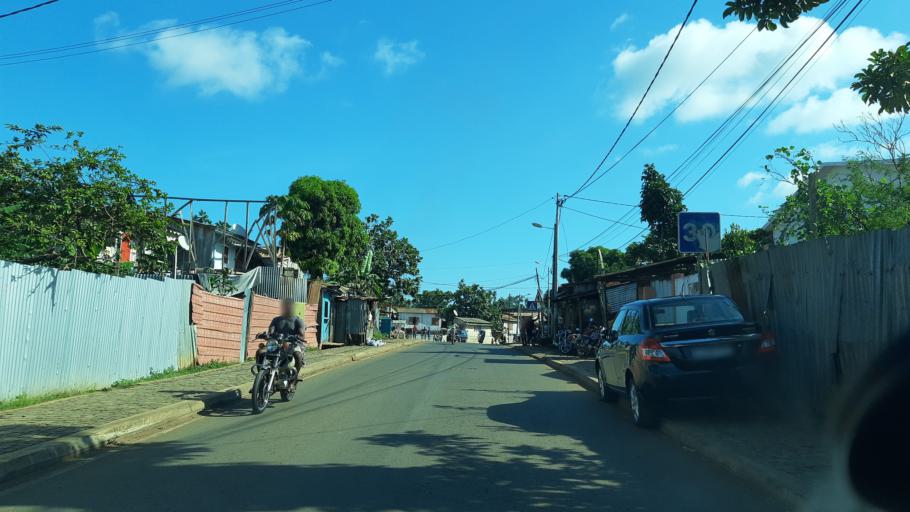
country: ST
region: Sao Tome Island
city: Sao Tome
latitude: 0.3241
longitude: 6.7279
